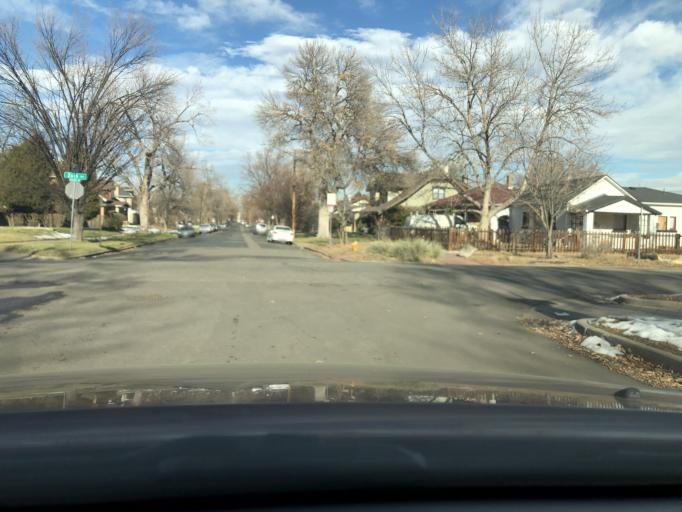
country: US
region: Colorado
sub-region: Denver County
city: Denver
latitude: 39.7543
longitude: -104.9610
